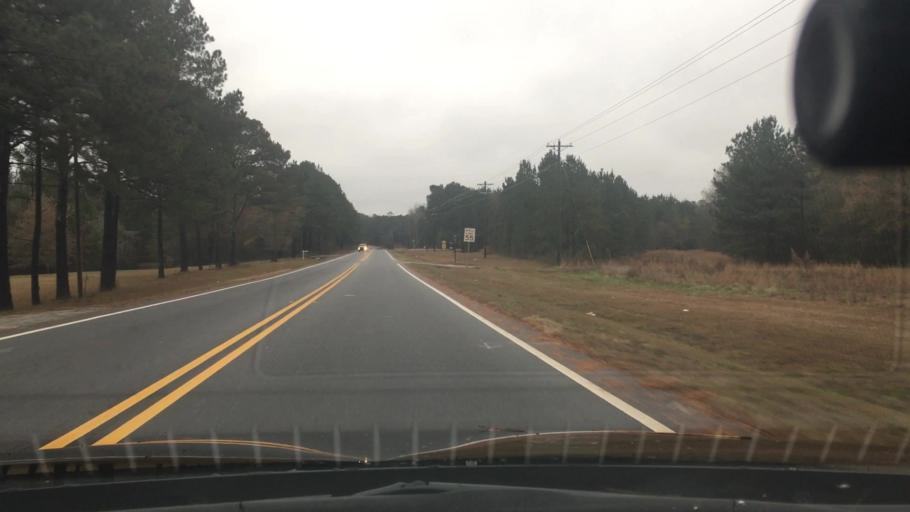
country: US
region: Georgia
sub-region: Coweta County
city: Senoia
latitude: 33.2675
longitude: -84.5233
